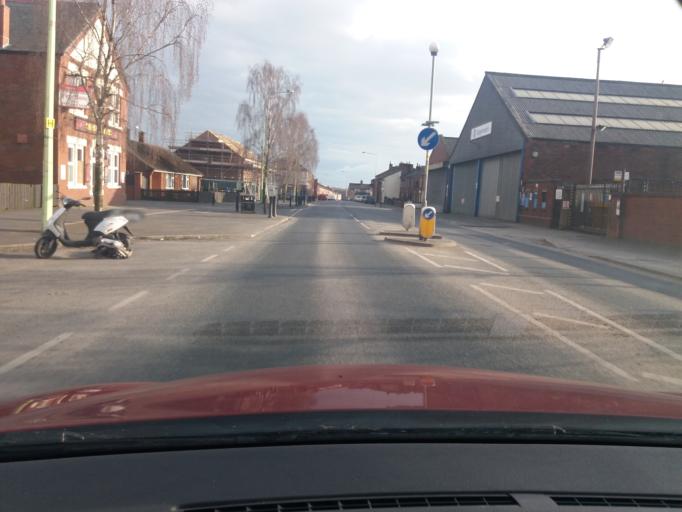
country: GB
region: England
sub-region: Lancashire
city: Chorley
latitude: 53.6515
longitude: -2.6176
